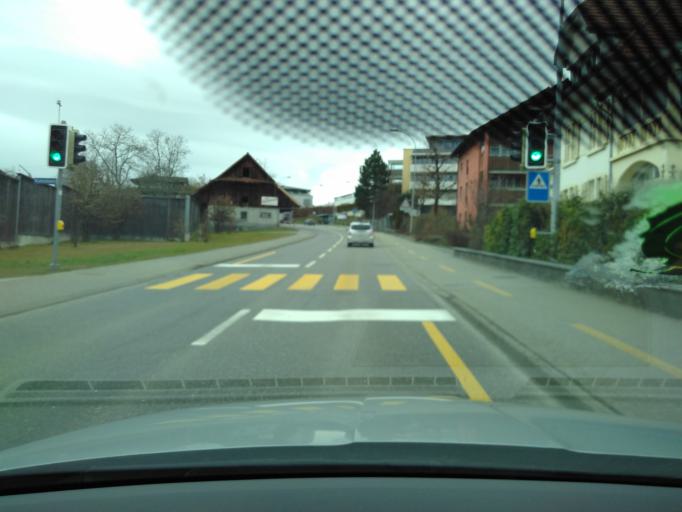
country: CH
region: Lucerne
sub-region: Hochdorf District
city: Emmen
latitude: 47.0964
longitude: 8.2720
